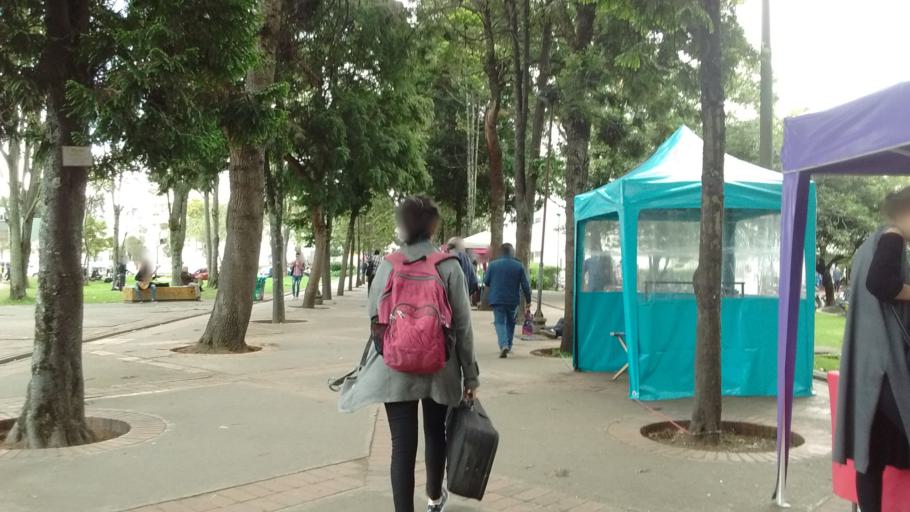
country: CO
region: Bogota D.C.
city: Bogota
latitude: 4.6351
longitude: -74.0808
